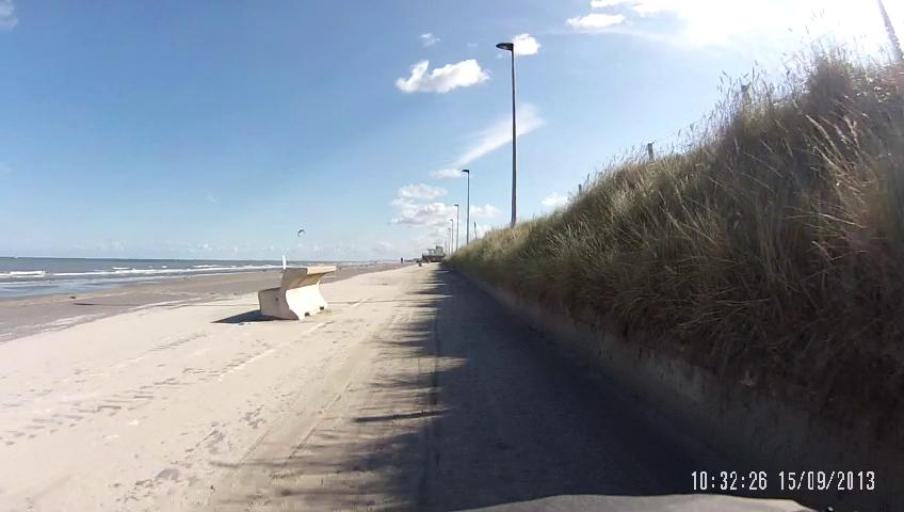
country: FR
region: Nord-Pas-de-Calais
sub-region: Departement du Nord
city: Coudekerque-Branche
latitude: 51.0552
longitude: 2.4208
